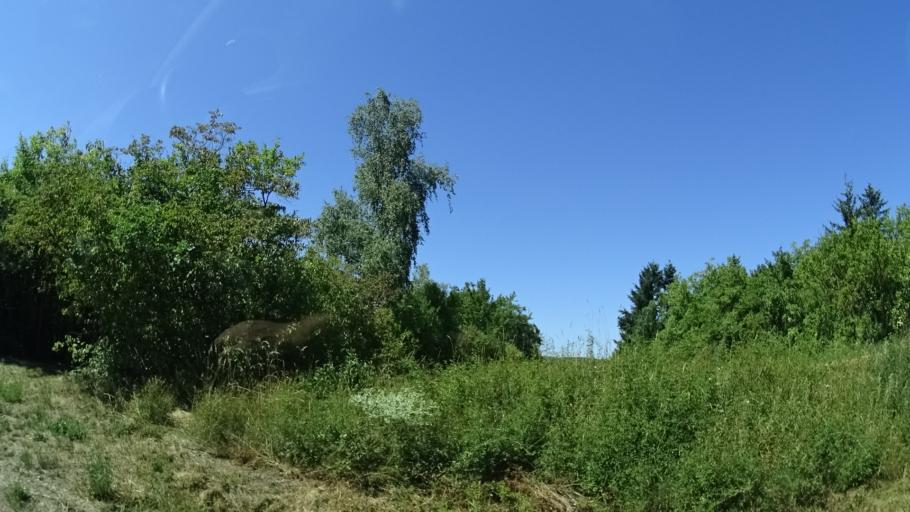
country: DE
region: Bavaria
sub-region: Regierungsbezirk Unterfranken
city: Veitshochheim
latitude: 49.8258
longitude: 9.8834
